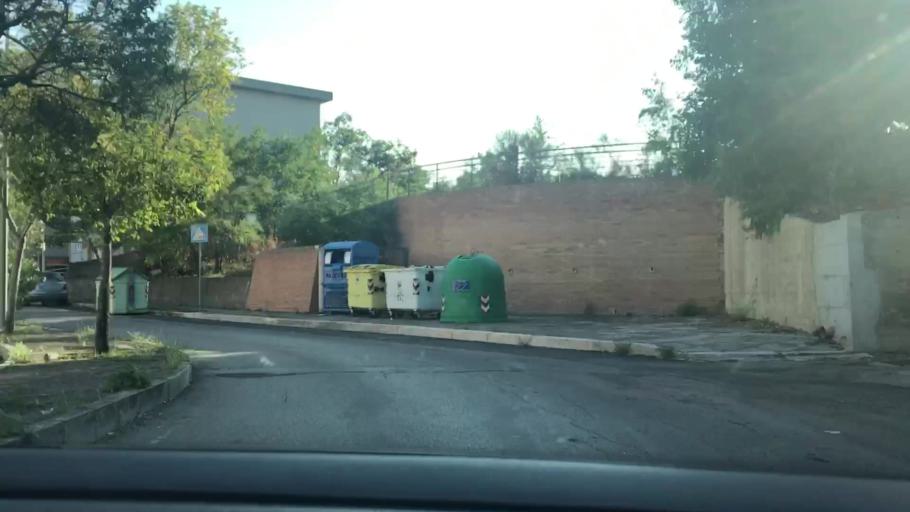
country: IT
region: Basilicate
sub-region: Provincia di Matera
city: Matera
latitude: 40.6858
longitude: 16.5849
